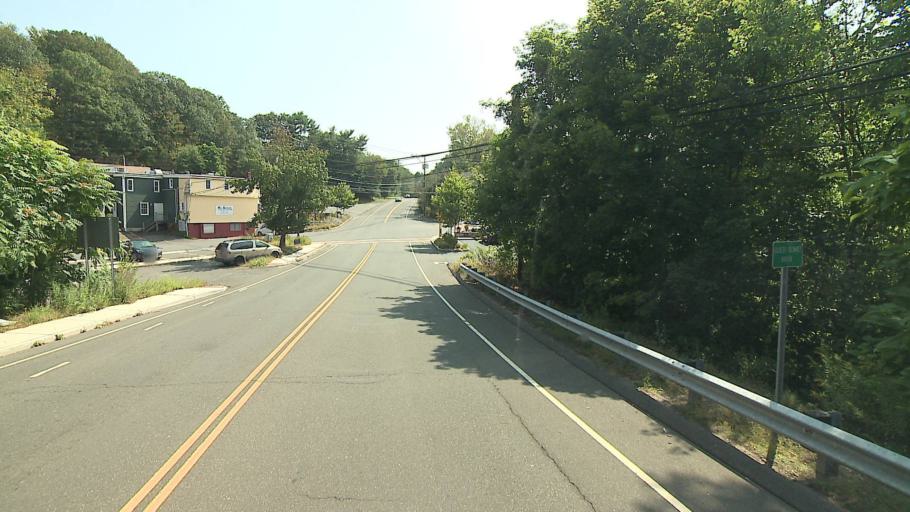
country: US
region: Connecticut
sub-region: Fairfield County
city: Georgetown
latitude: 41.2572
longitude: -73.4281
